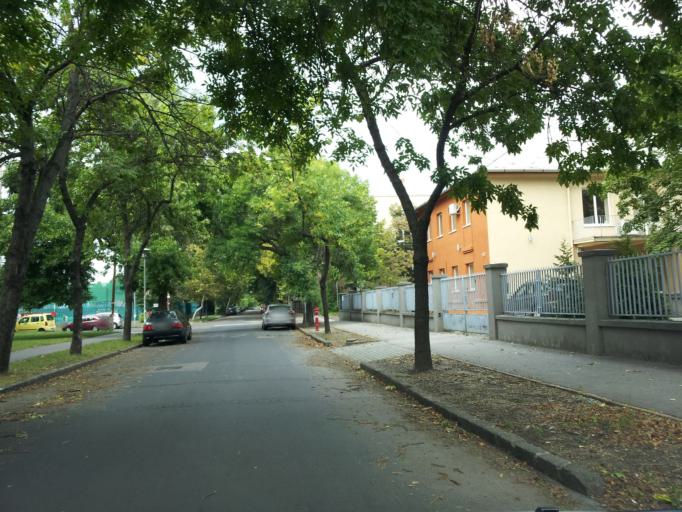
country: HU
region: Budapest
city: Budapest XI. keruelet
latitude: 47.4634
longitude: 19.0406
